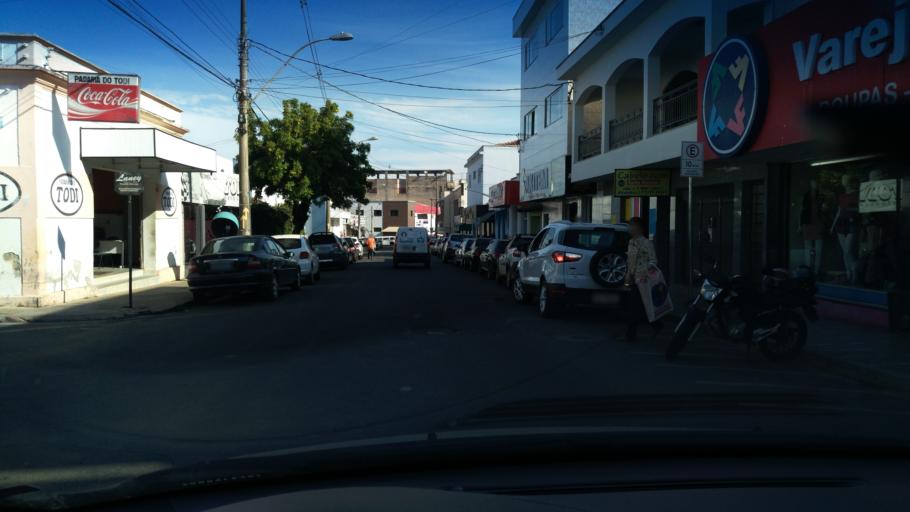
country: BR
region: Minas Gerais
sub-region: Andradas
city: Andradas
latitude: -22.0742
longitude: -46.5740
